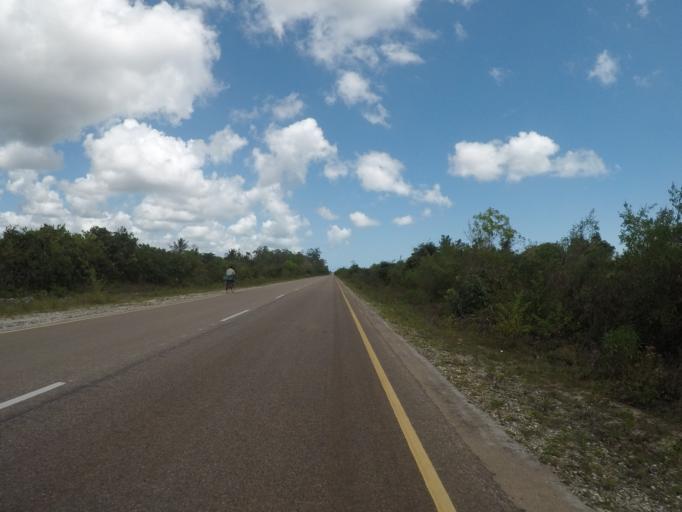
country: TZ
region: Zanzibar Central/South
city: Koani
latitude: -6.2531
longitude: 39.3560
